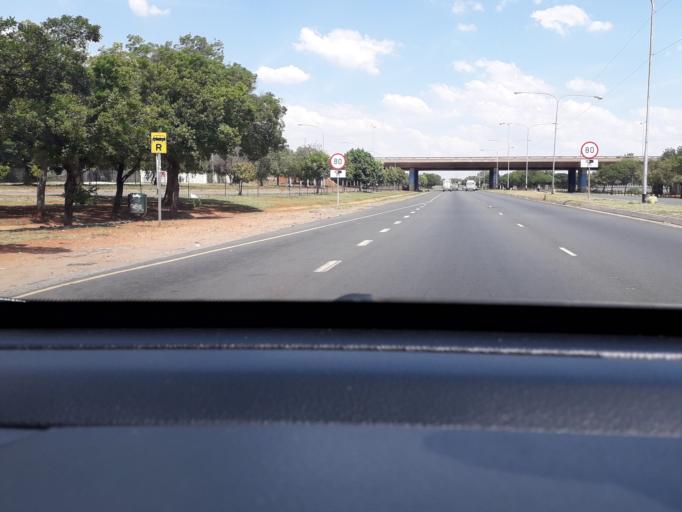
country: ZA
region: Gauteng
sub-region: City of Tshwane Metropolitan Municipality
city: Centurion
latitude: -25.8157
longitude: 28.2027
